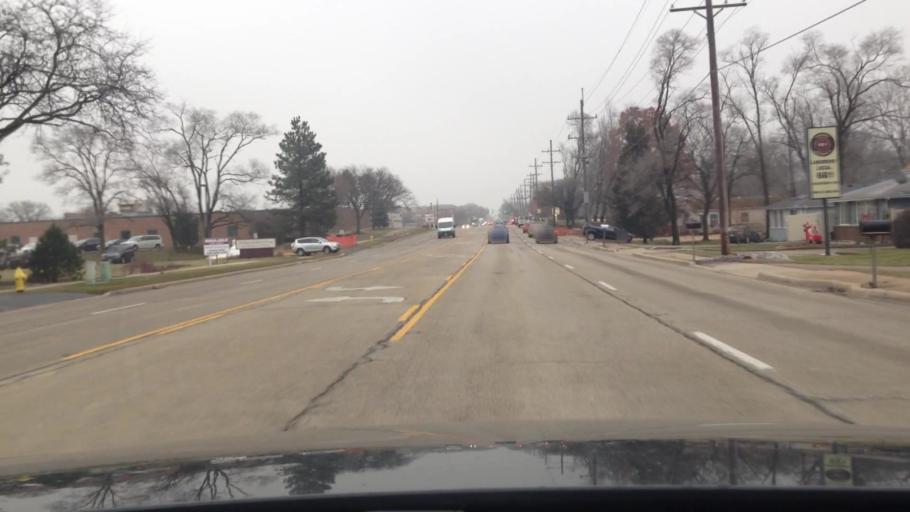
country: US
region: Illinois
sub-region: DuPage County
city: Westmont
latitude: 41.8150
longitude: -87.9761
